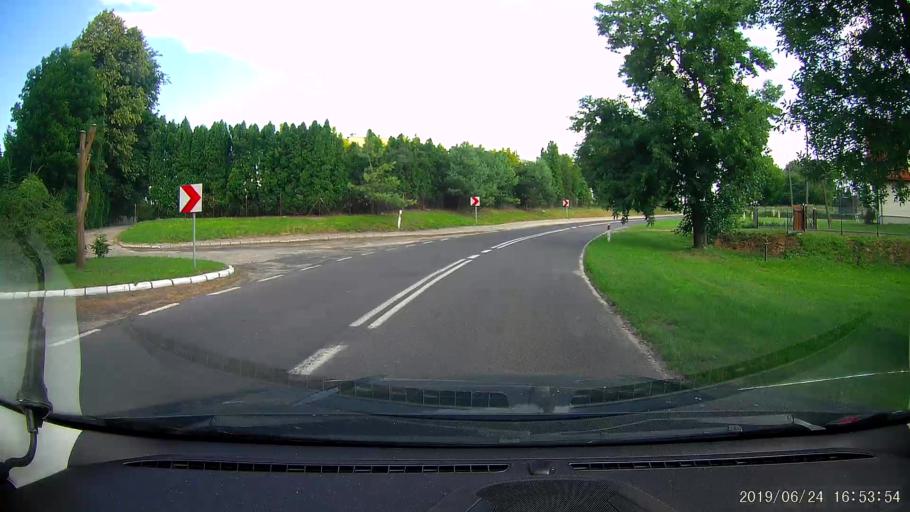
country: PL
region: Lublin Voivodeship
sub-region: Powiat tomaszowski
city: Telatyn
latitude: 50.5340
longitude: 23.8075
